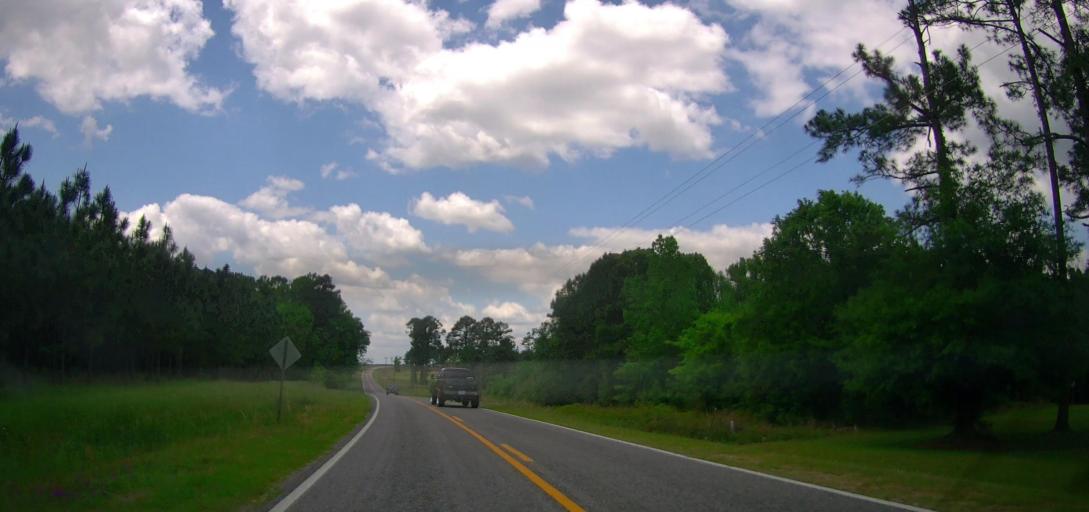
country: US
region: Georgia
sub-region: Laurens County
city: East Dublin
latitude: 32.5396
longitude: -82.8112
